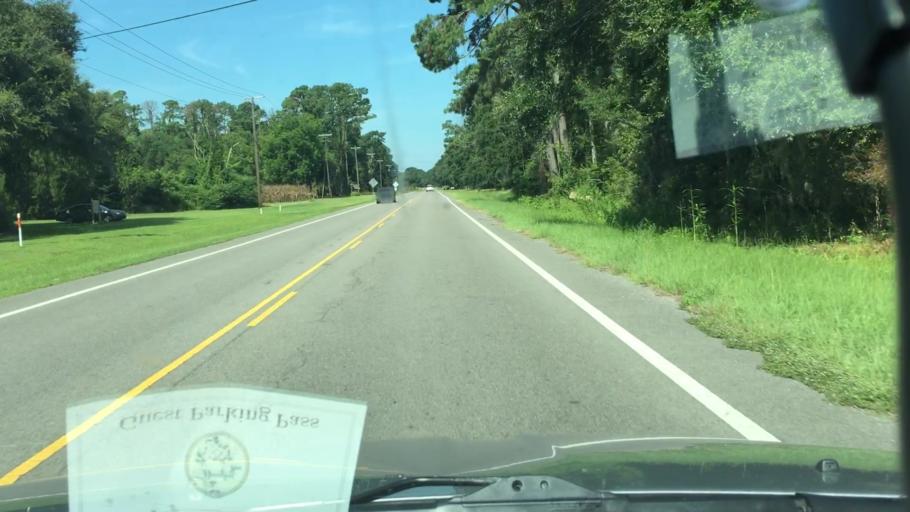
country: US
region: South Carolina
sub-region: Beaufort County
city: Beaufort
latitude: 32.4130
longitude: -80.5099
